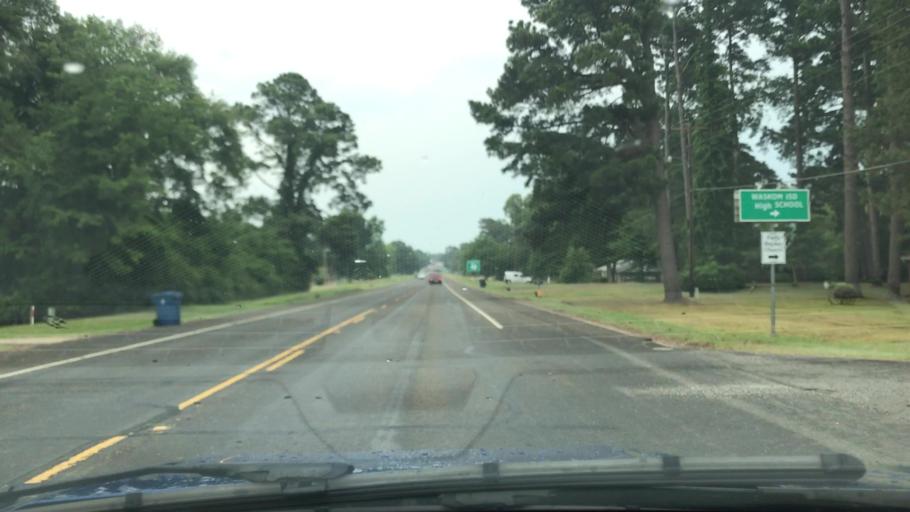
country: US
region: Texas
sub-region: Harrison County
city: Waskom
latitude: 32.4792
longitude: -94.0755
